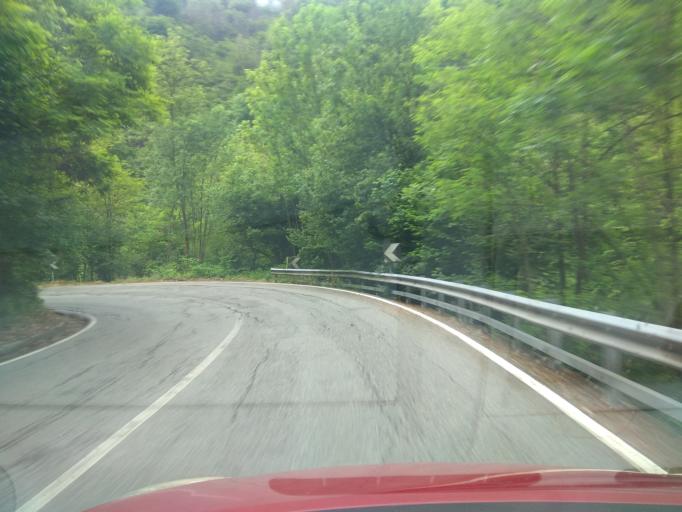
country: IT
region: Piedmont
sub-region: Provincia di Biella
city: Pray
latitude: 45.6627
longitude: 8.2021
